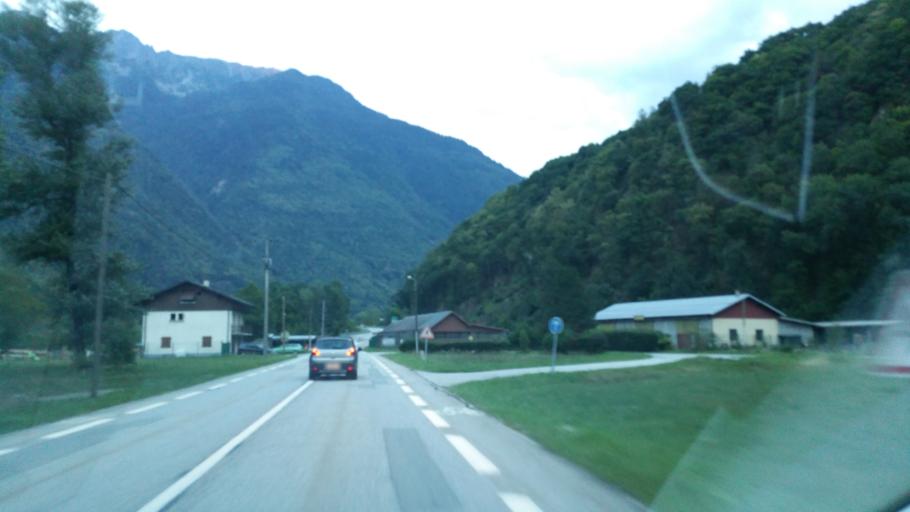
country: FR
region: Rhone-Alpes
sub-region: Departement de la Savoie
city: Saint-Remy-de-Maurienne
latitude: 45.4634
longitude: 6.2891
